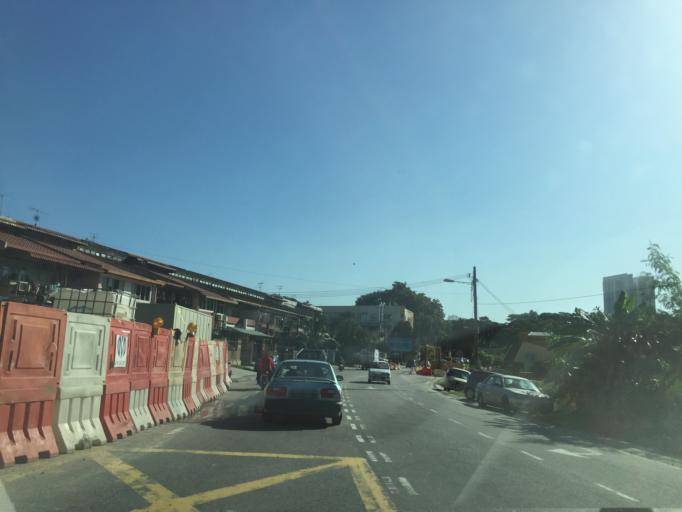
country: MY
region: Selangor
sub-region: Petaling
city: Petaling Jaya
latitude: 3.1188
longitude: 101.6274
